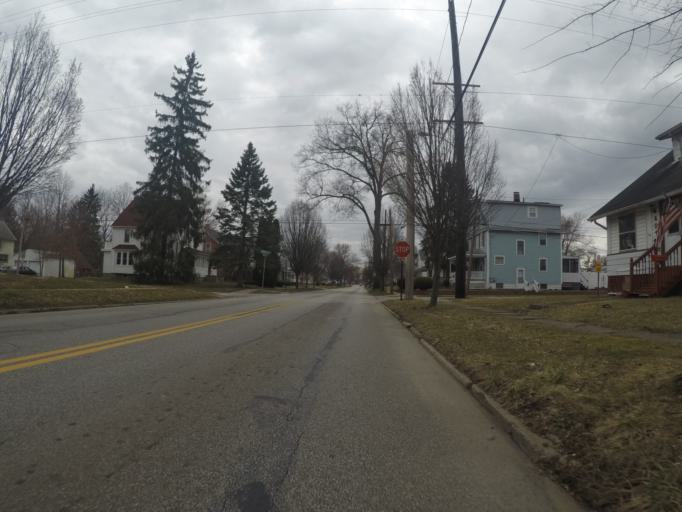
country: US
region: Ohio
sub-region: Portage County
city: Ravenna
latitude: 41.1553
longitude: -81.2537
